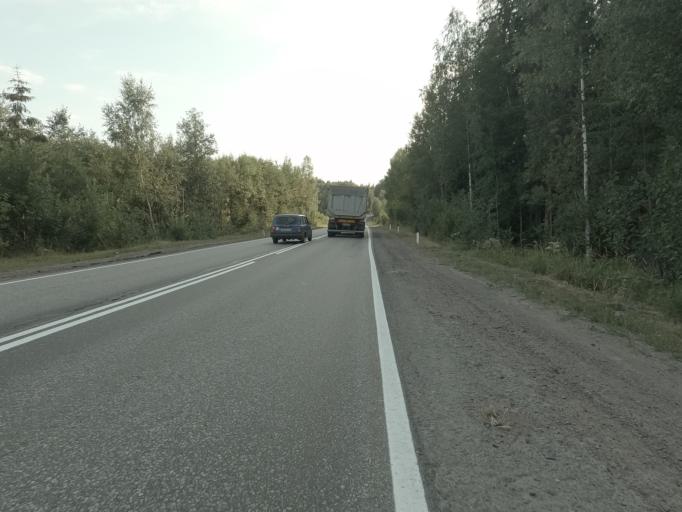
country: RU
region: Leningrad
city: Vyborg
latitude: 60.8457
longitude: 28.8564
